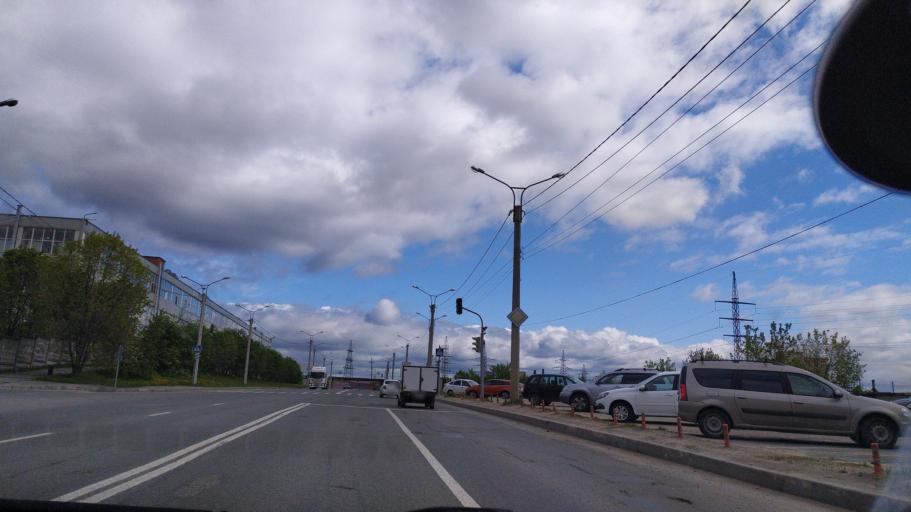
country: RU
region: Chuvashia
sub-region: Cheboksarskiy Rayon
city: Cheboksary
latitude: 56.1147
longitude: 47.2990
